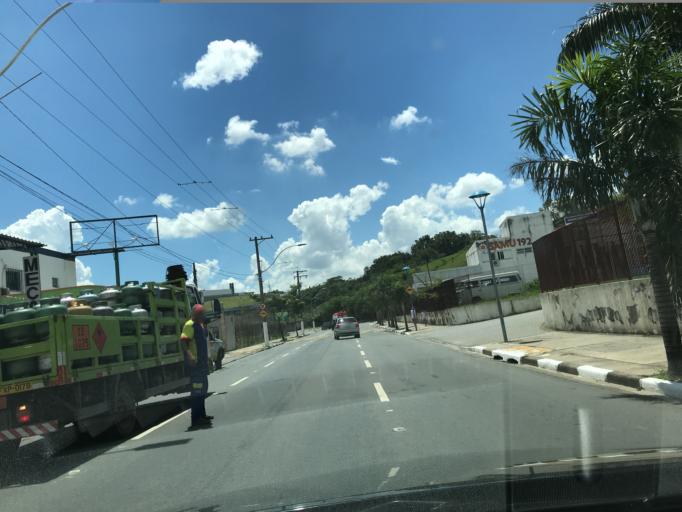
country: BR
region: Sao Paulo
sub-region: Itapevi
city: Itapevi
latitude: -23.5401
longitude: -46.9341
